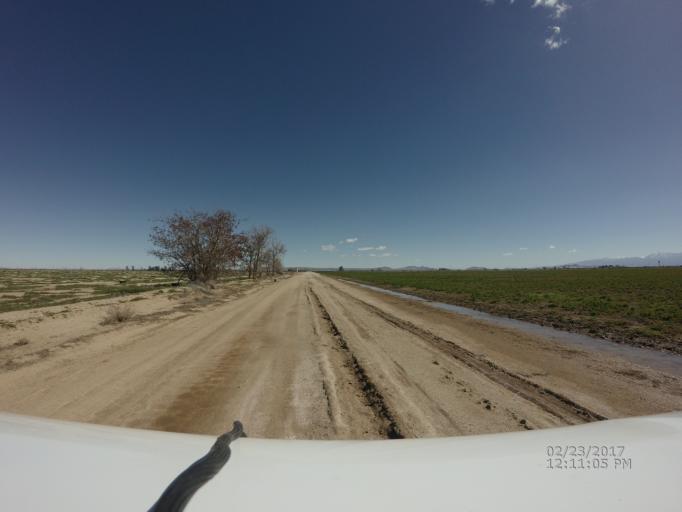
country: US
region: California
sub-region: Los Angeles County
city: Lancaster
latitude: 34.7413
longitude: -118.0137
